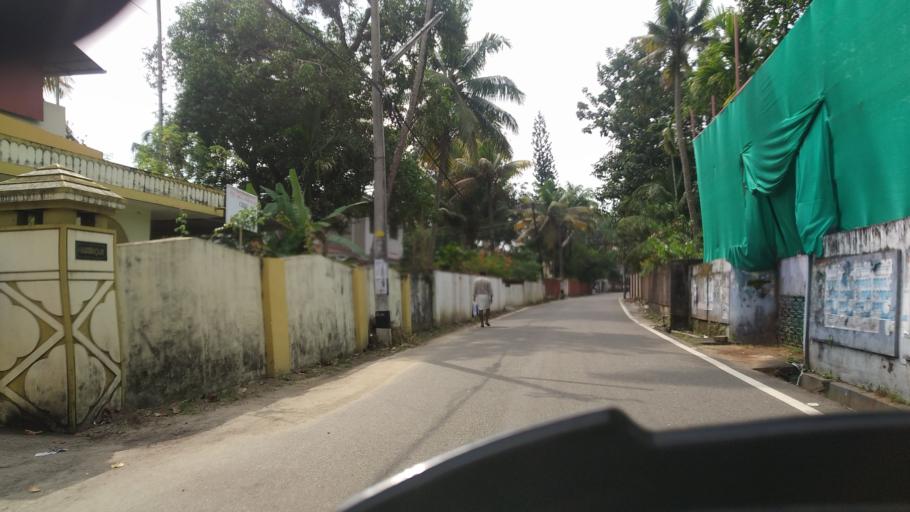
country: IN
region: Kerala
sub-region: Thrissur District
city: Kodungallur
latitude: 10.1437
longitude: 76.2328
